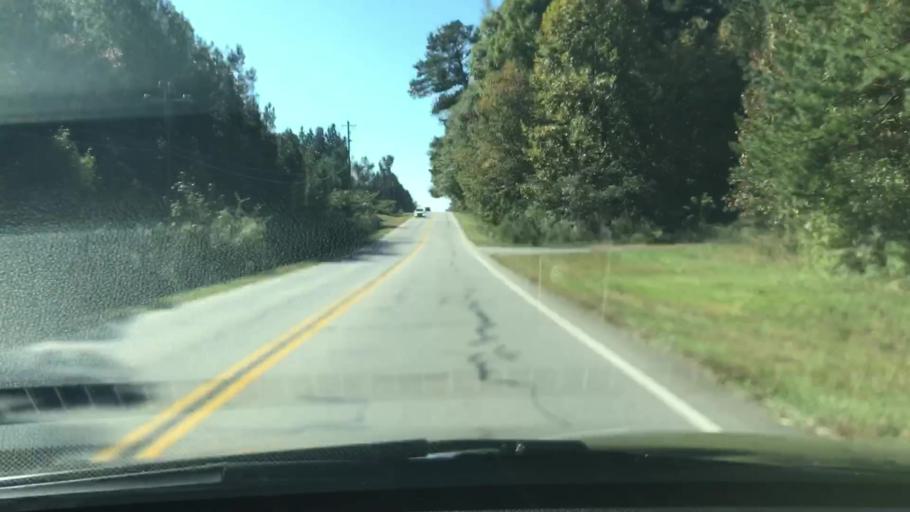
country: US
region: Georgia
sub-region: Carroll County
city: Villa Rica
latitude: 33.7698
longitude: -84.8995
